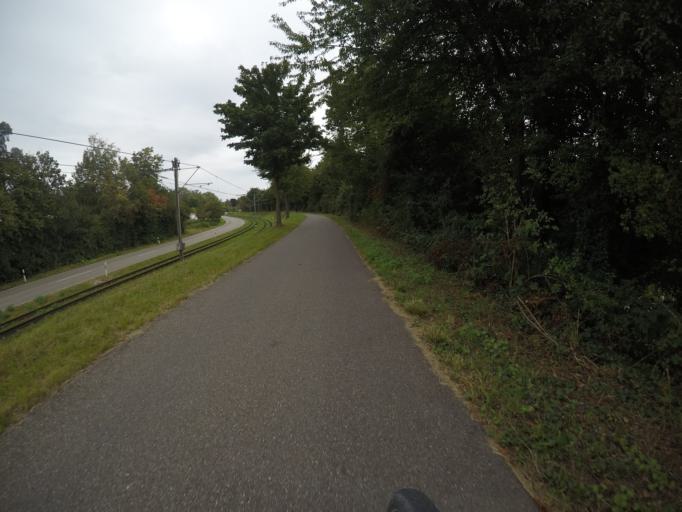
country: DE
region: Baden-Wuerttemberg
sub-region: Regierungsbezirk Stuttgart
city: Stuttgart Muehlhausen
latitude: 48.8697
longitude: 9.2636
